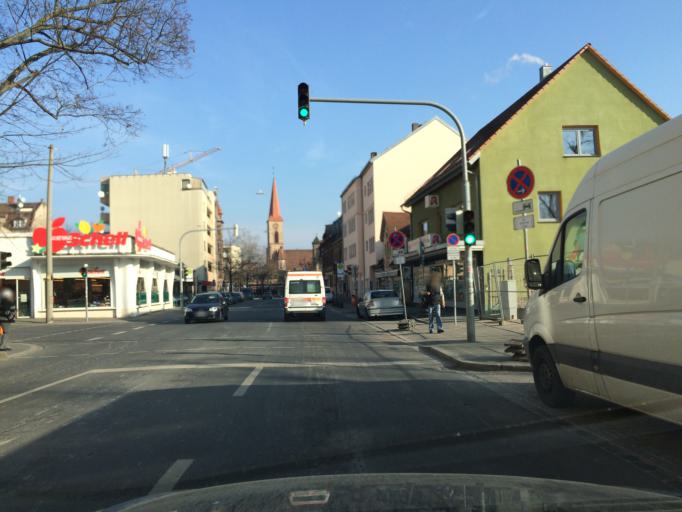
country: DE
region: Bavaria
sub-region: Regierungsbezirk Mittelfranken
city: Grossreuth bei Schweinau
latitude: 49.4379
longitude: 11.0512
